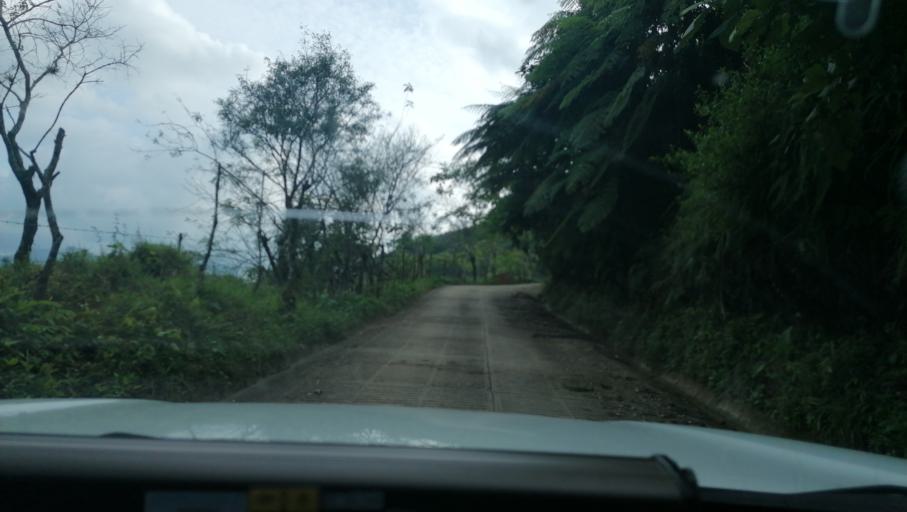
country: MX
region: Chiapas
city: Ixtacomitan
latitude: 17.3364
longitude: -93.1090
